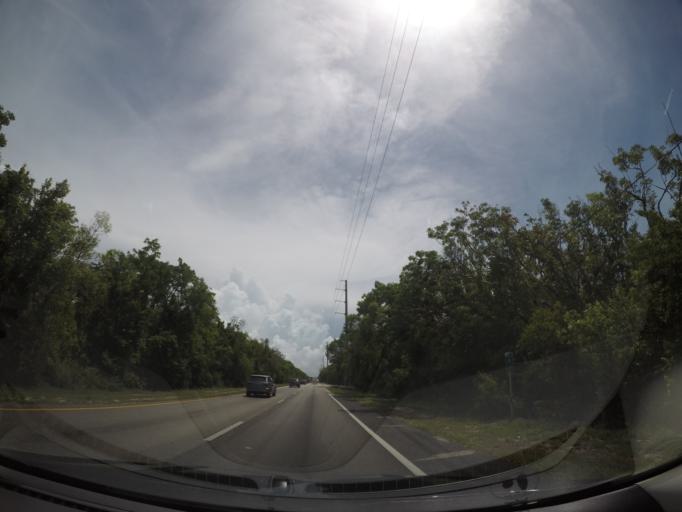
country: US
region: Florida
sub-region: Monroe County
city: Key Largo
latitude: 25.0670
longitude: -80.4693
